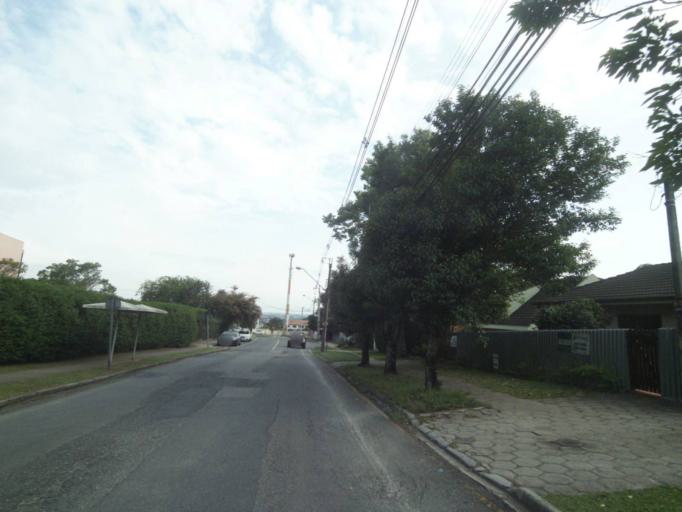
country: BR
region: Parana
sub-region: Curitiba
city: Curitiba
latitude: -25.4213
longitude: -49.3196
